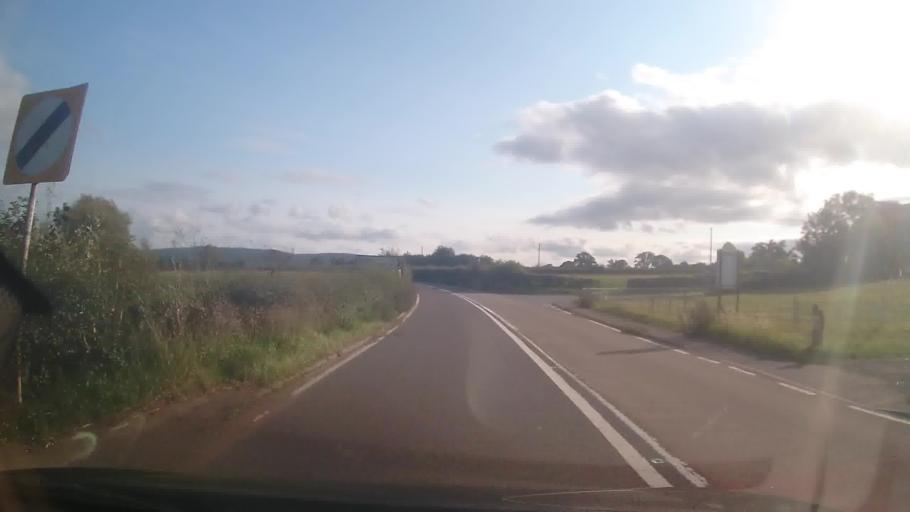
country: GB
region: England
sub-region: Shropshire
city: Bromfield
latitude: 52.4062
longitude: -2.8041
